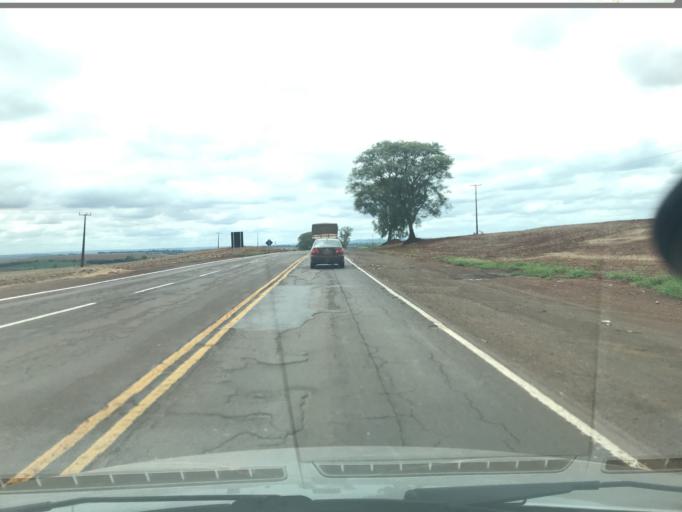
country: BR
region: Parana
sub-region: Terra Boa
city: Terra Boa
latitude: -23.6047
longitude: -52.4123
